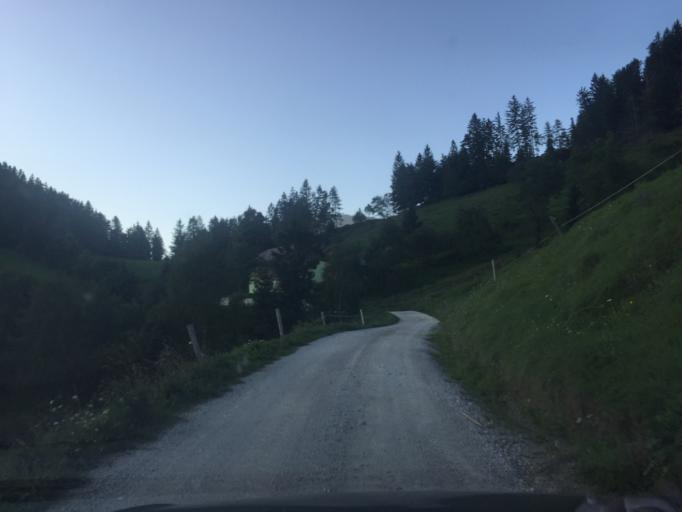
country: SI
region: Ravne na Koroskem
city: Kotlje
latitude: 46.4574
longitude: 14.9807
